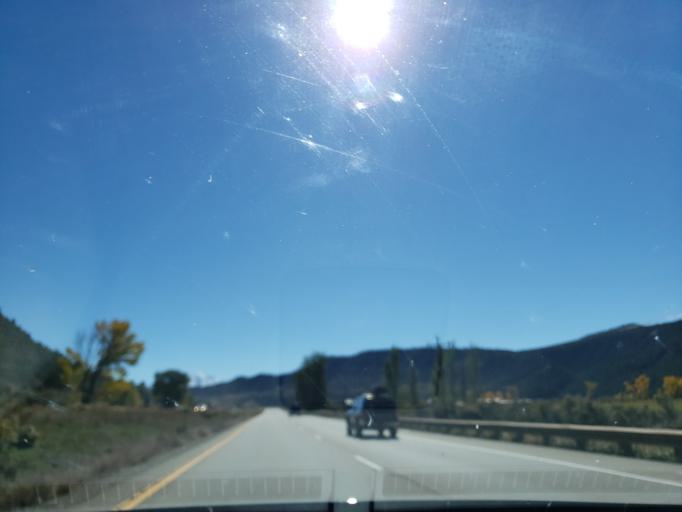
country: US
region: Colorado
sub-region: Garfield County
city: Glenwood Springs
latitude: 39.4927
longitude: -107.2995
